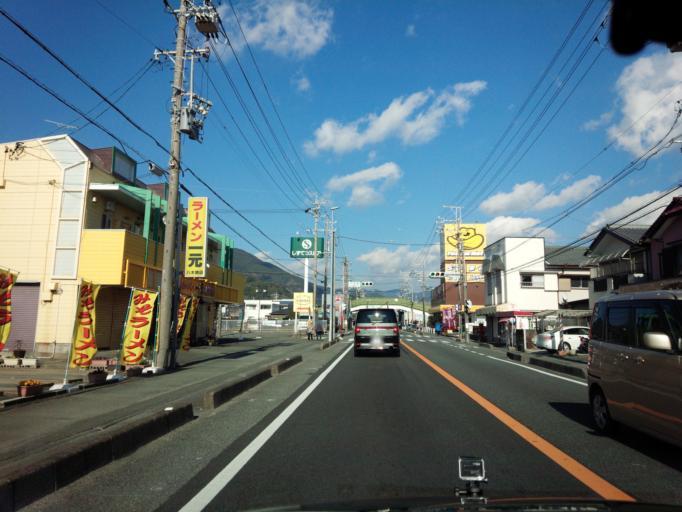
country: JP
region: Shizuoka
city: Shizuoka-shi
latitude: 35.0643
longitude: 138.5240
